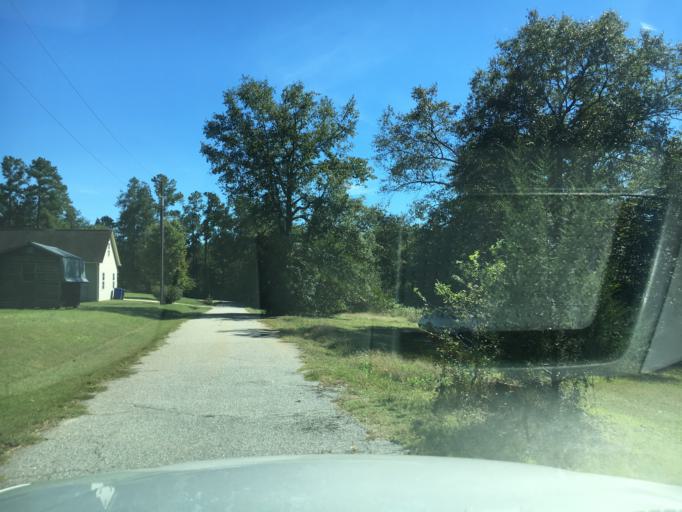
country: US
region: South Carolina
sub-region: Spartanburg County
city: Duncan
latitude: 34.9424
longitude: -82.1555
